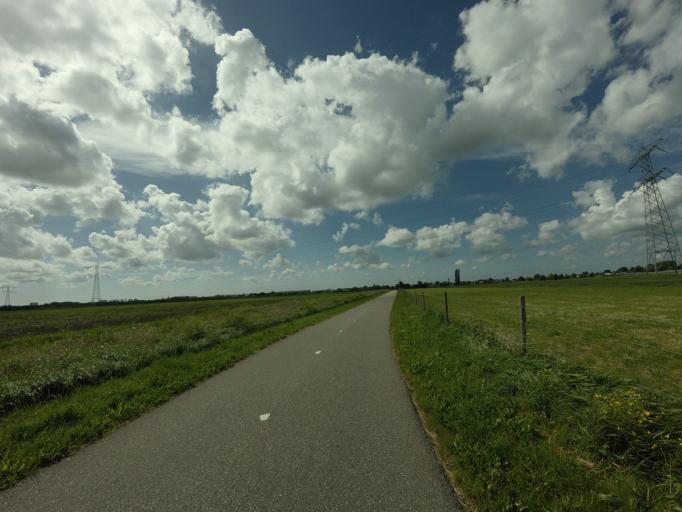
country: NL
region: North Holland
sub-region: Gemeente Hoorn
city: Hoorn
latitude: 52.6811
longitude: 5.0617
